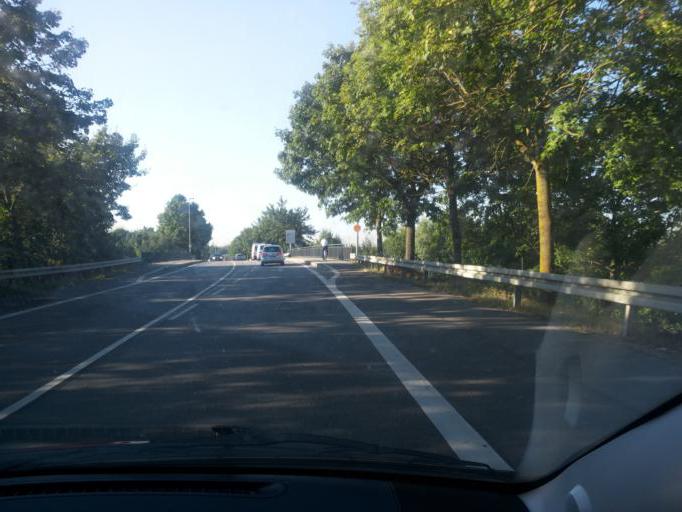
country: DE
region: Bavaria
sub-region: Upper Bavaria
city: Wettstetten
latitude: 48.7927
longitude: 11.4023
